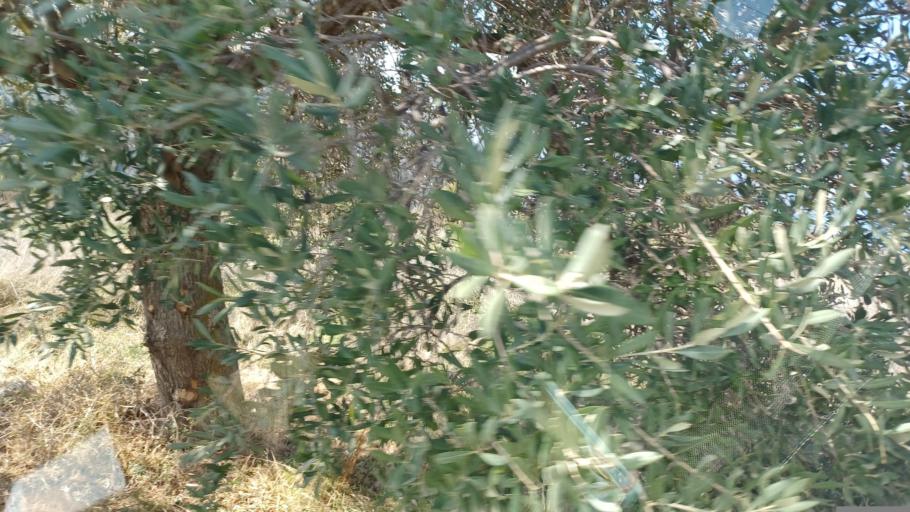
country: CY
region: Pafos
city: Polis
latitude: 35.0315
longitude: 32.5035
